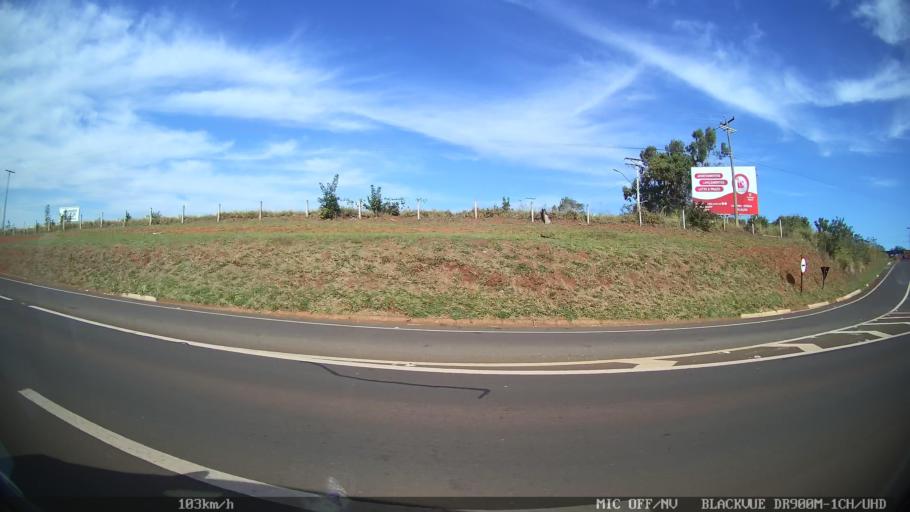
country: BR
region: Sao Paulo
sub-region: Araraquara
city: Araraquara
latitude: -21.7952
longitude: -48.1352
